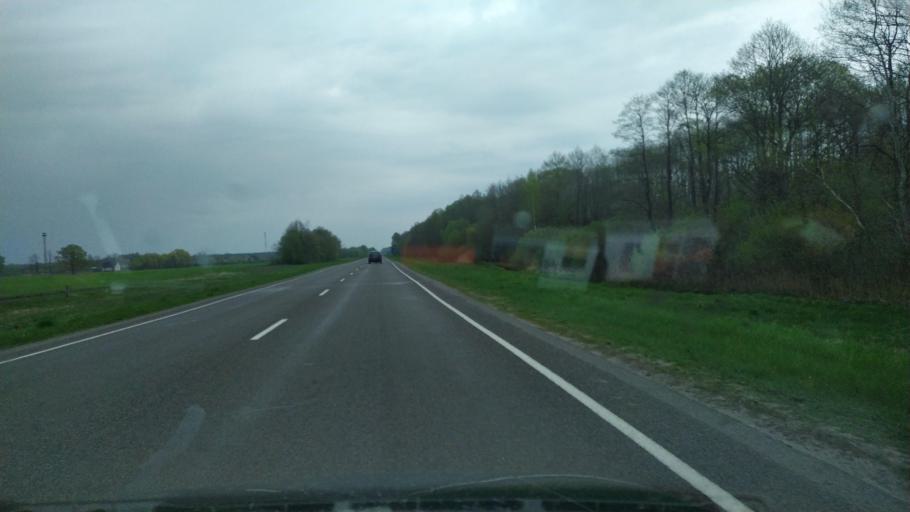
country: BY
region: Brest
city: Horad Kobryn
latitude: 52.3204
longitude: 24.5592
